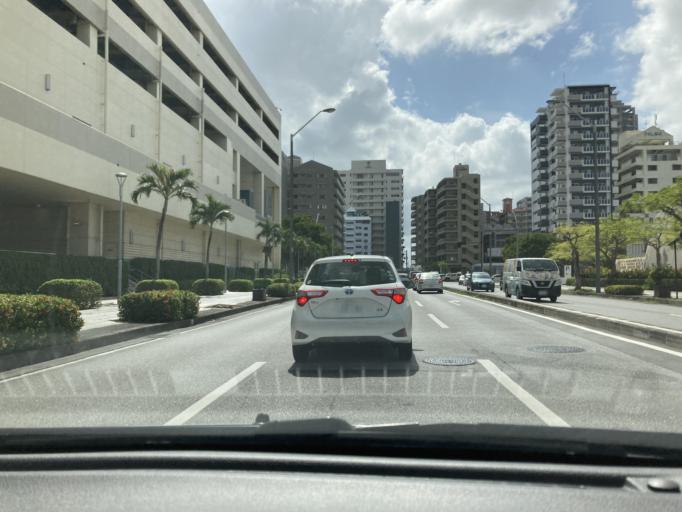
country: JP
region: Okinawa
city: Naha-shi
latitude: 26.2265
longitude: 127.6945
